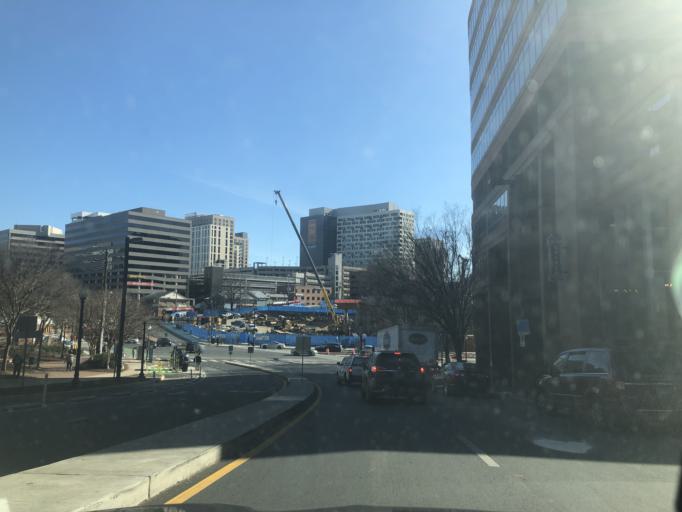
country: US
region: Maryland
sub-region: Montgomery County
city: Silver Spring
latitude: 38.9954
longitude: -77.0313
